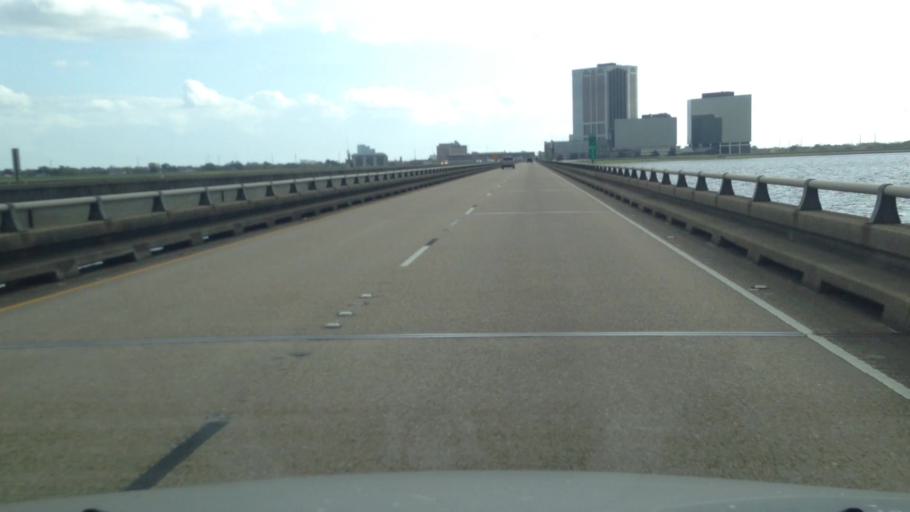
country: US
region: Louisiana
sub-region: Jefferson Parish
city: Metairie
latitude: 30.0295
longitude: -90.1528
